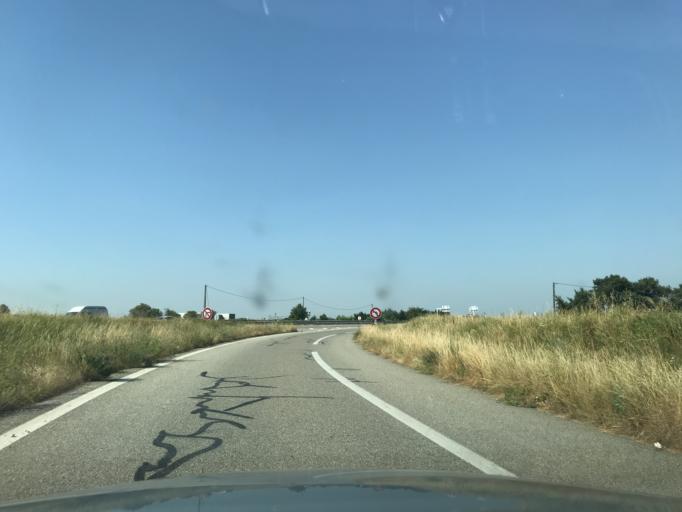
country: FR
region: Rhone-Alpes
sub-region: Departement de la Drome
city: Saint-Marcel-les-Valence
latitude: 44.9866
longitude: 4.9816
